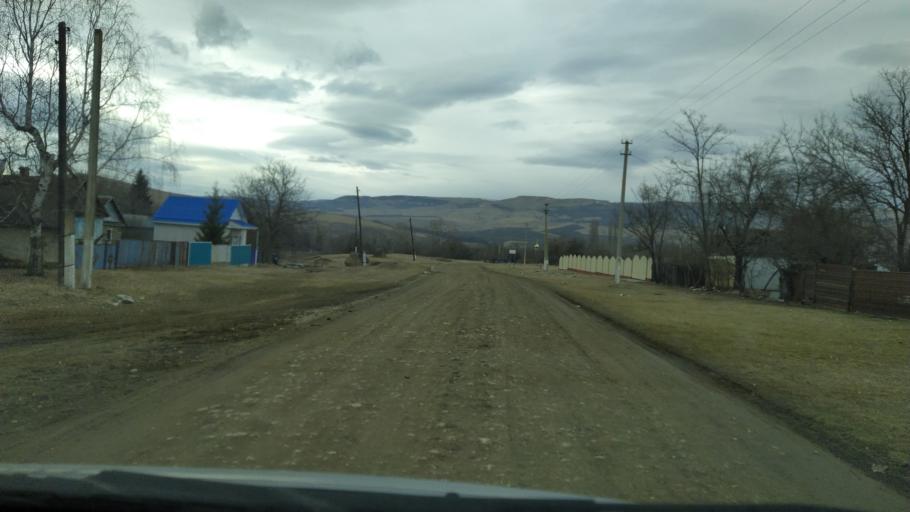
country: RU
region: Krasnodarskiy
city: Peredovaya
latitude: 44.0840
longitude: 41.3660
